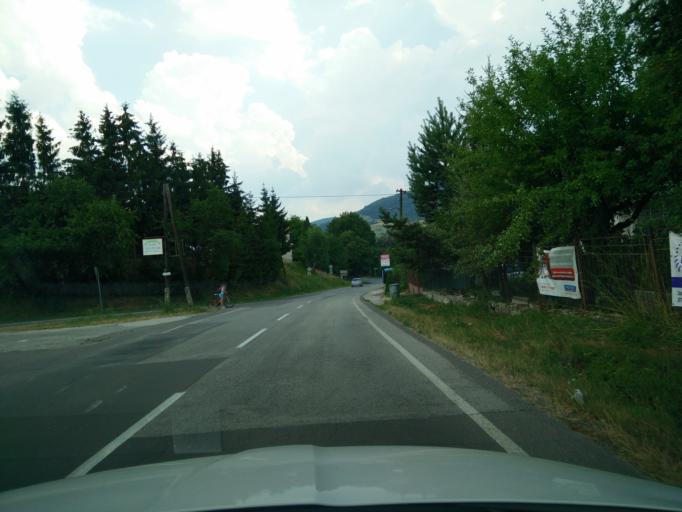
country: SK
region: Nitriansky
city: Novaky
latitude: 48.8012
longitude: 18.4764
